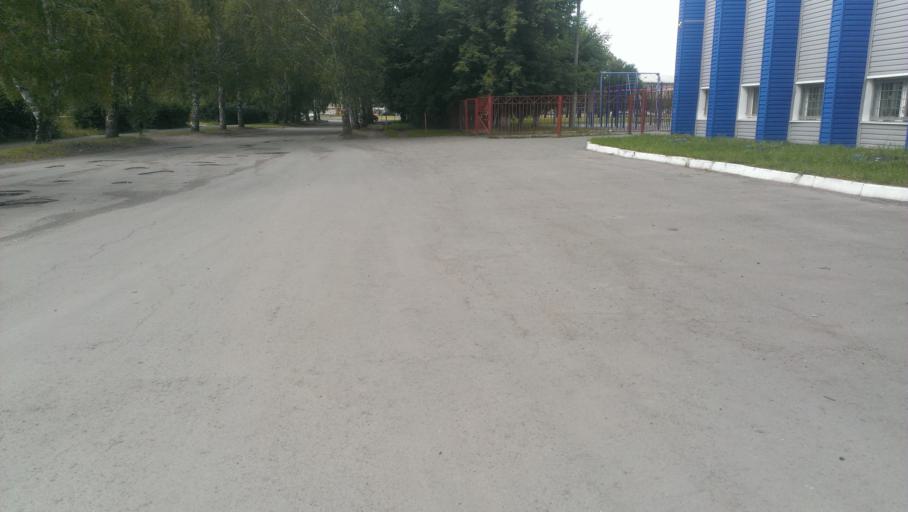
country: RU
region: Altai Krai
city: Yuzhnyy
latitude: 53.2525
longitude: 83.6926
